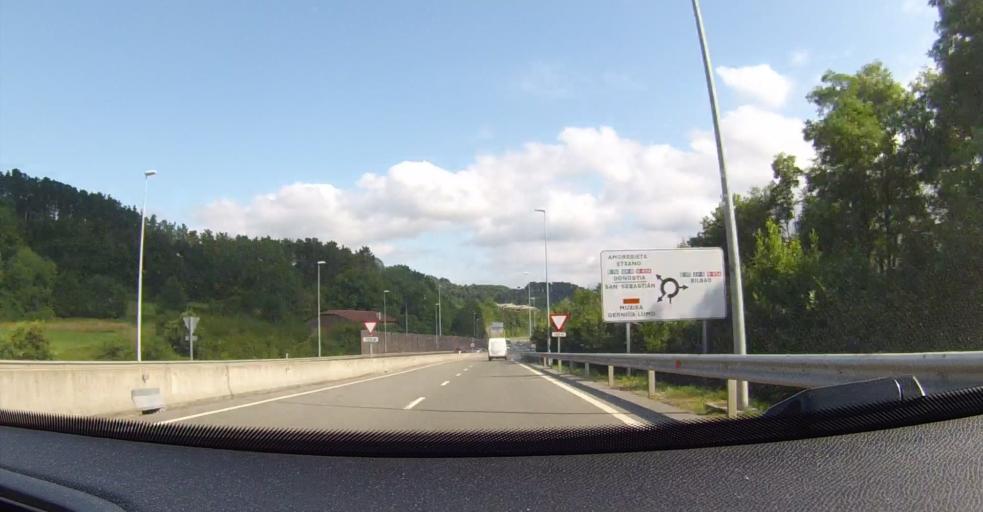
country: ES
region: Basque Country
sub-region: Bizkaia
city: Amorebieta
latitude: 43.2254
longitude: -2.7297
